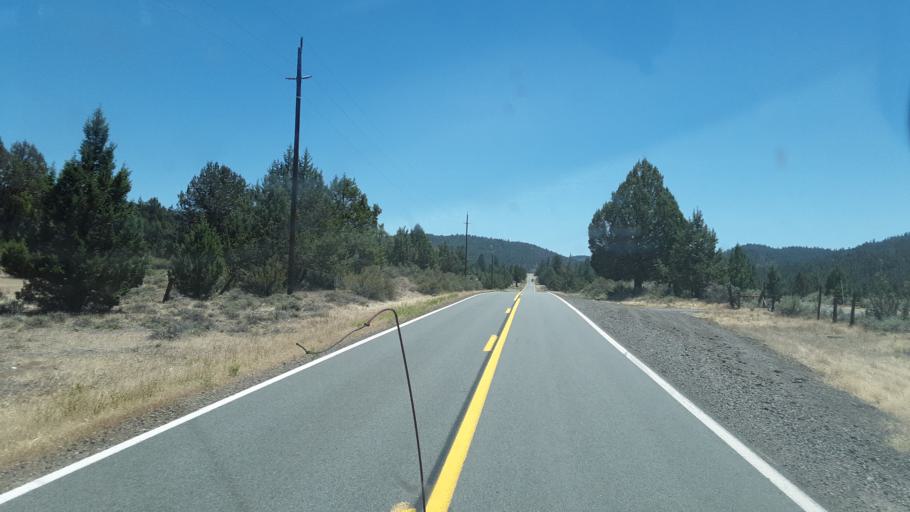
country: US
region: California
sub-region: Modoc County
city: Alturas
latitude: 41.0583
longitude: -120.8757
